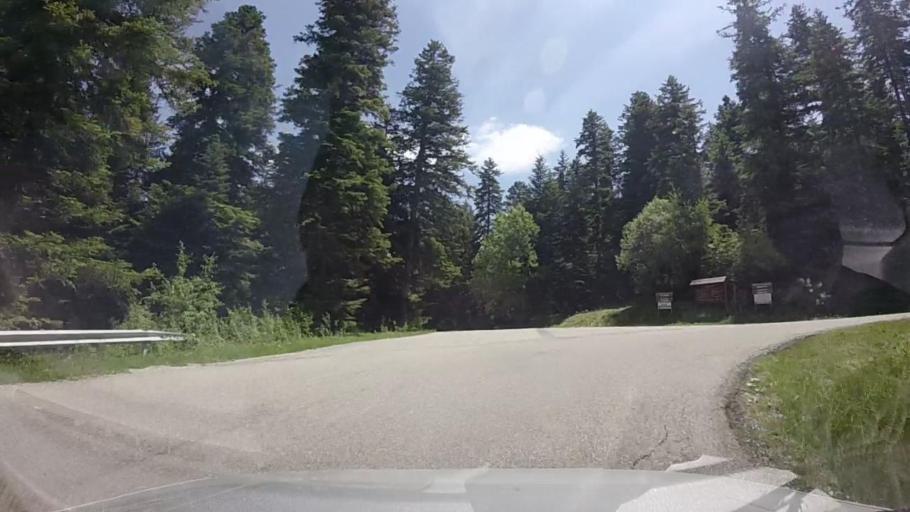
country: FR
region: Provence-Alpes-Cote d'Azur
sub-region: Departement des Alpes-de-Haute-Provence
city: Seyne-les-Alpes
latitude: 44.3496
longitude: 6.3011
